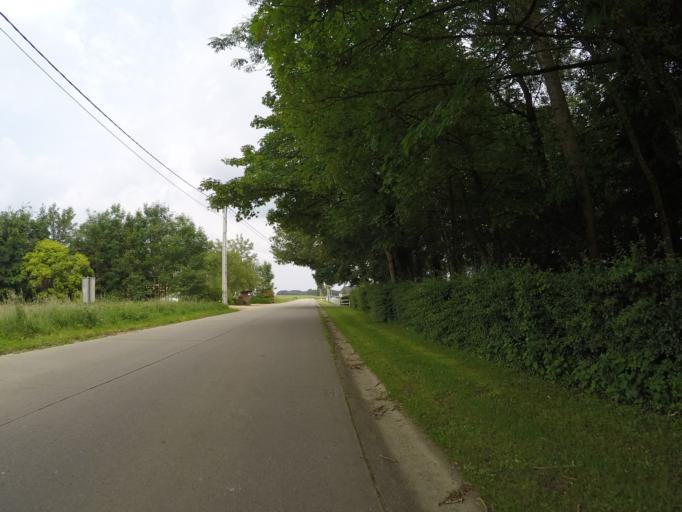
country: BE
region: Wallonia
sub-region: Province de Namur
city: Assesse
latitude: 50.3390
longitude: 4.9866
